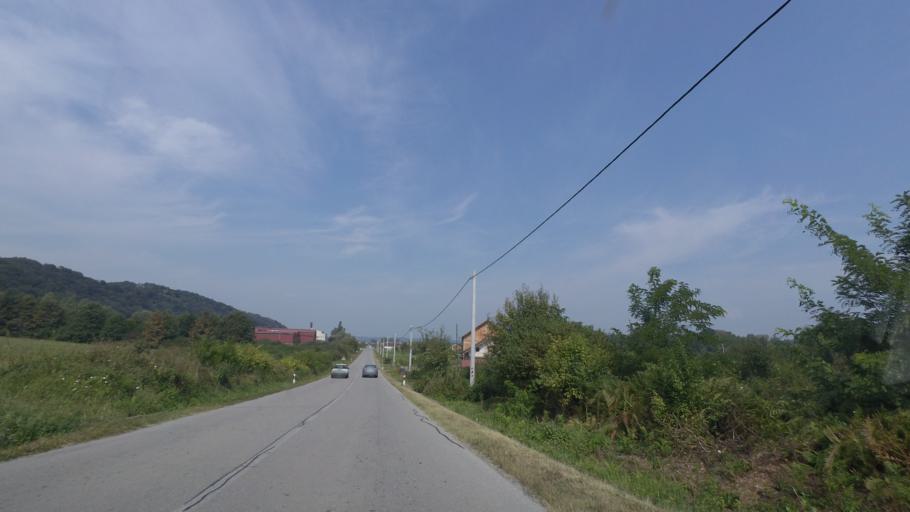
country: HR
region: Sisacko-Moslavacka
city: Glina
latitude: 45.3168
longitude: 16.1118
